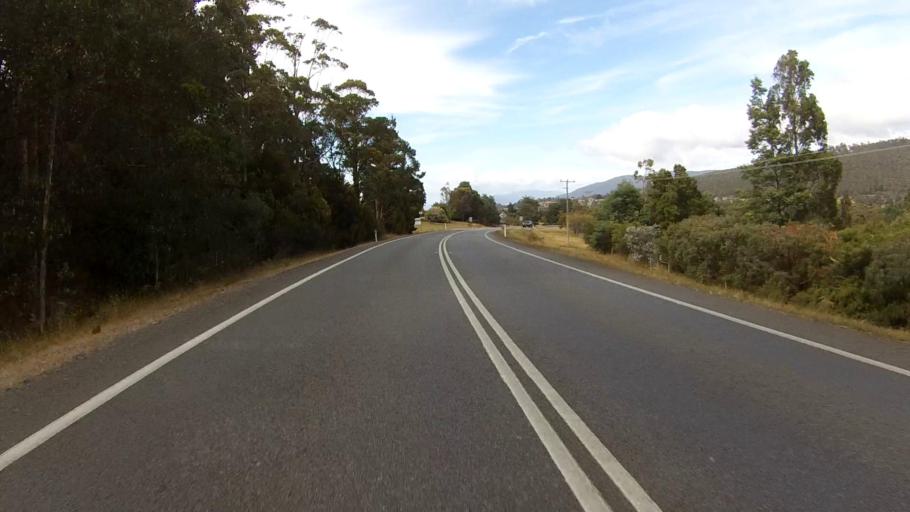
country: AU
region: Tasmania
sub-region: Kingborough
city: Kettering
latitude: -43.1140
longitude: 147.2448
